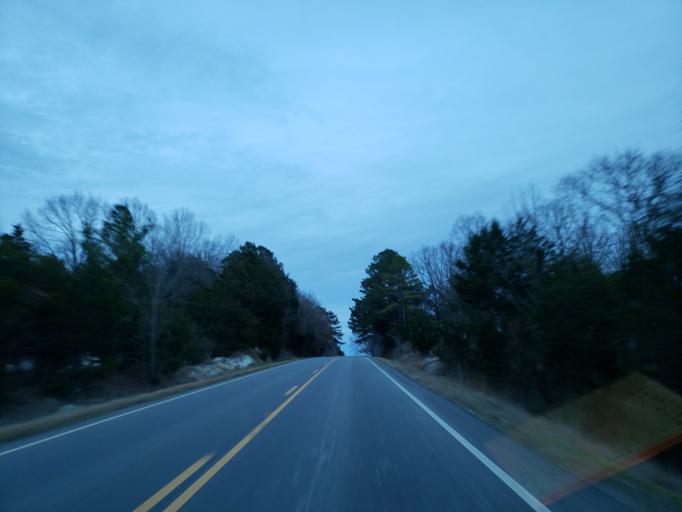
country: US
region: Alabama
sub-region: Sumter County
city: Livingston
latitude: 32.8113
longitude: -88.2560
